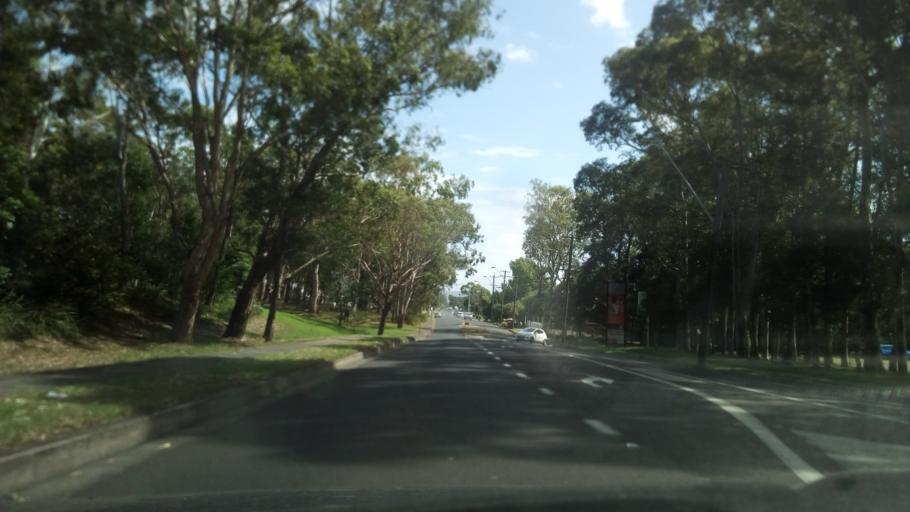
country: AU
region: New South Wales
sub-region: Wollongong
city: Gwynneville
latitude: -34.4190
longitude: 150.8847
